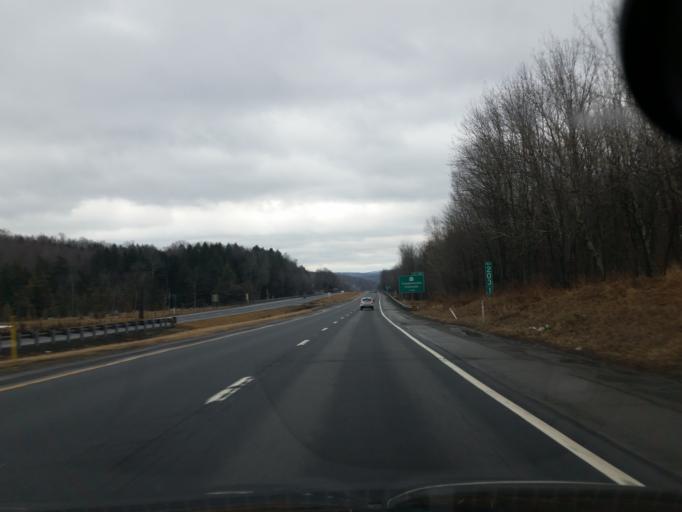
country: US
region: Pennsylvania
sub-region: Lackawanna County
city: Dalton
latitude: 41.6101
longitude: -75.6455
